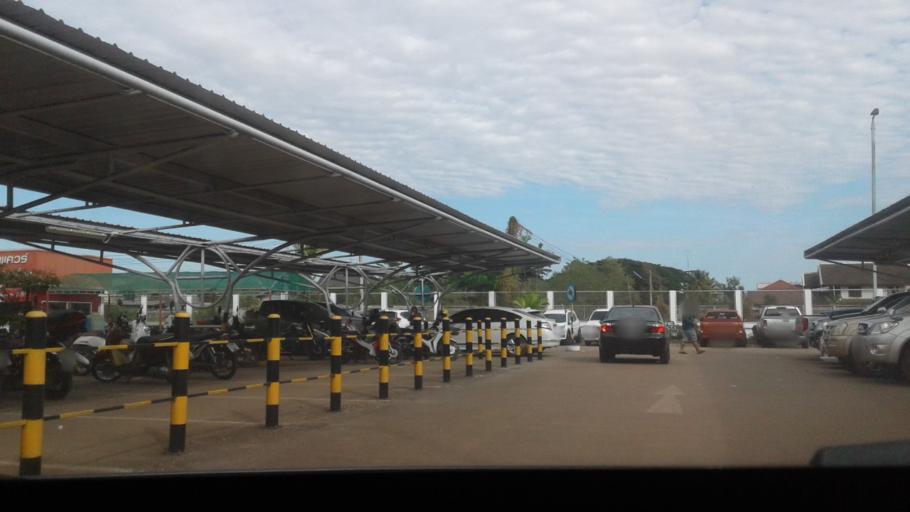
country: TH
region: Changwat Udon Thani
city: Udon Thani
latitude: 17.4308
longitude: 102.7876
